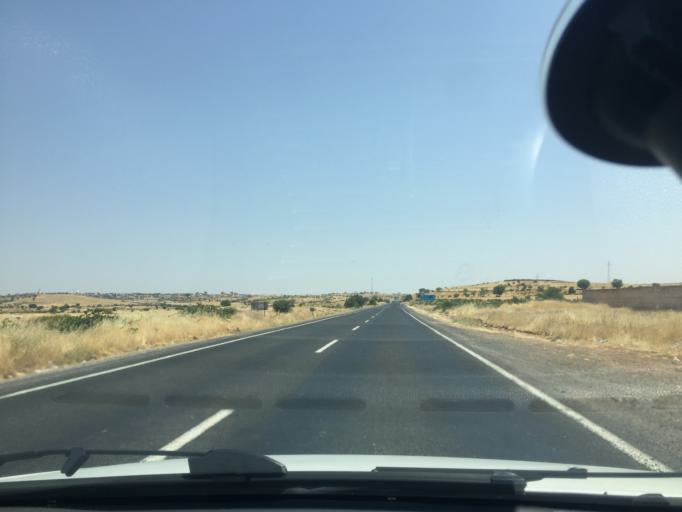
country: TR
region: Mardin
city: Acirli
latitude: 37.4512
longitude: 41.2627
